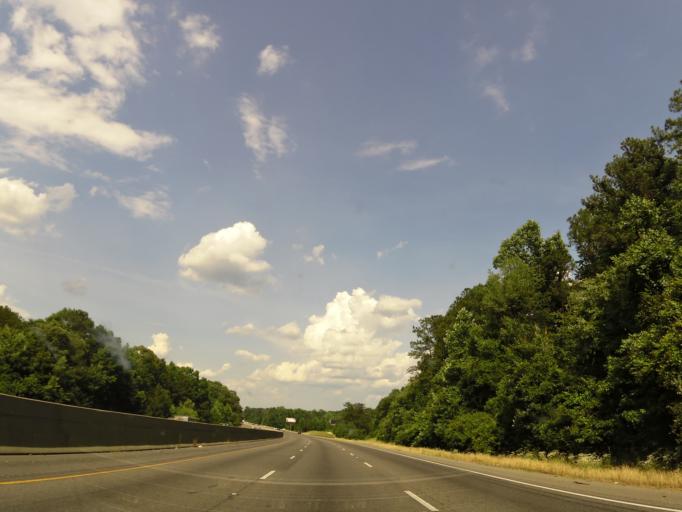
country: US
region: Alabama
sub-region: Tuscaloosa County
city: Coaling
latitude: 33.1774
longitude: -87.3812
